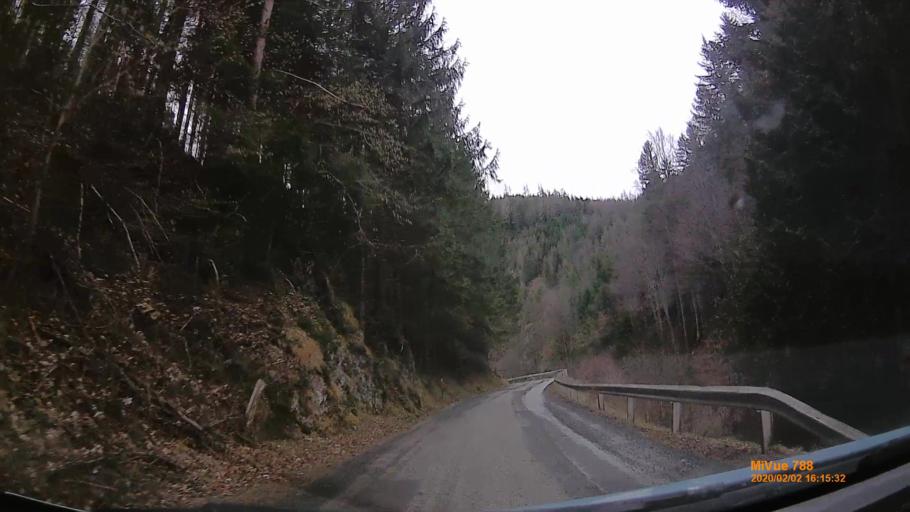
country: AT
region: Lower Austria
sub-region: Politischer Bezirk Neunkirchen
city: Semmering
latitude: 47.6558
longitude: 15.8176
